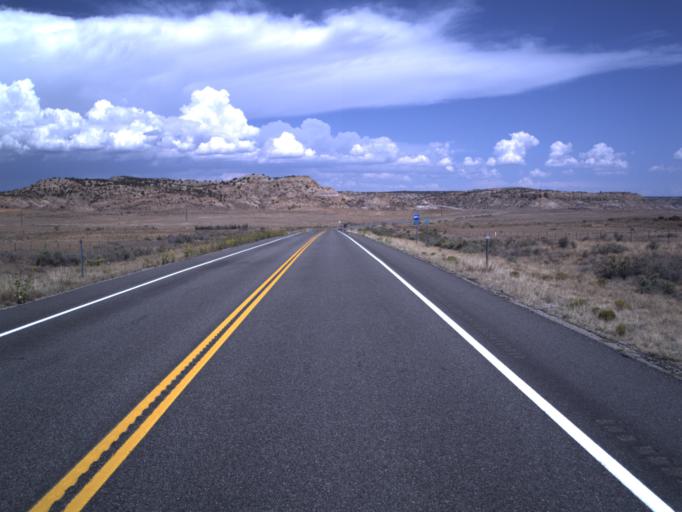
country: US
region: Utah
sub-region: San Juan County
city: Blanding
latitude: 37.4061
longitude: -109.4902
